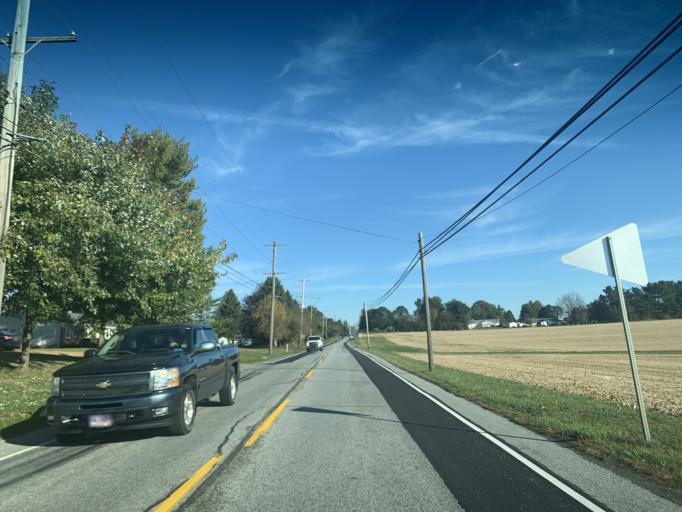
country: US
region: Pennsylvania
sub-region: Chester County
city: Parkesburg
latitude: 39.8844
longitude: -75.9224
